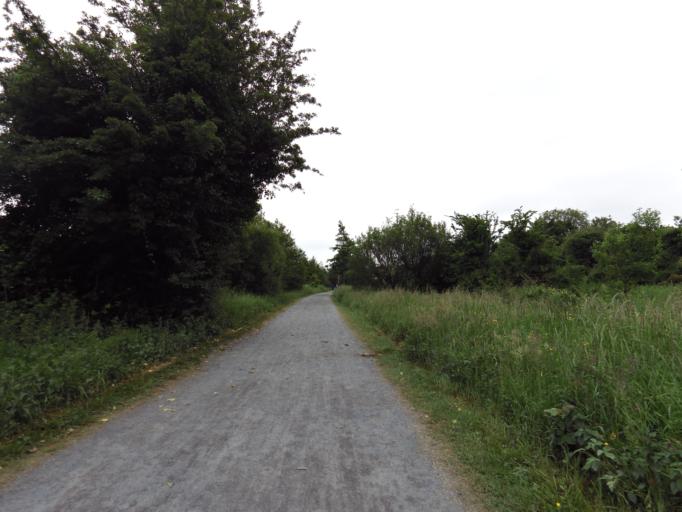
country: IE
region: Connaught
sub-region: County Galway
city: Gaillimh
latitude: 53.2906
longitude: -9.0665
